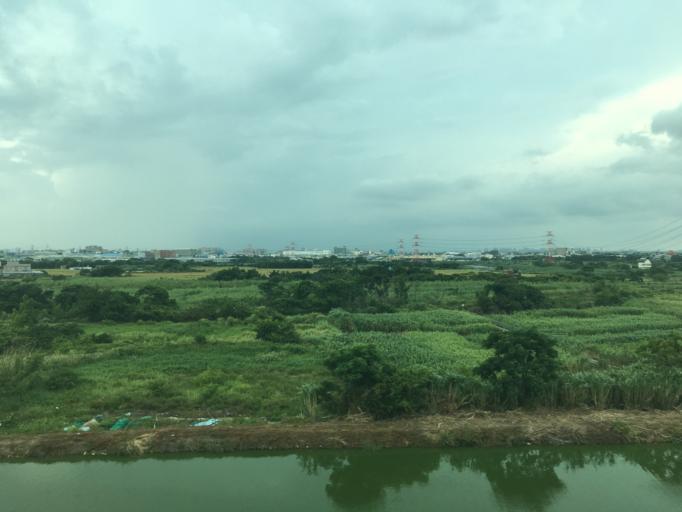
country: TW
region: Taiwan
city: Taoyuan City
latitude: 25.0820
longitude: 121.2764
